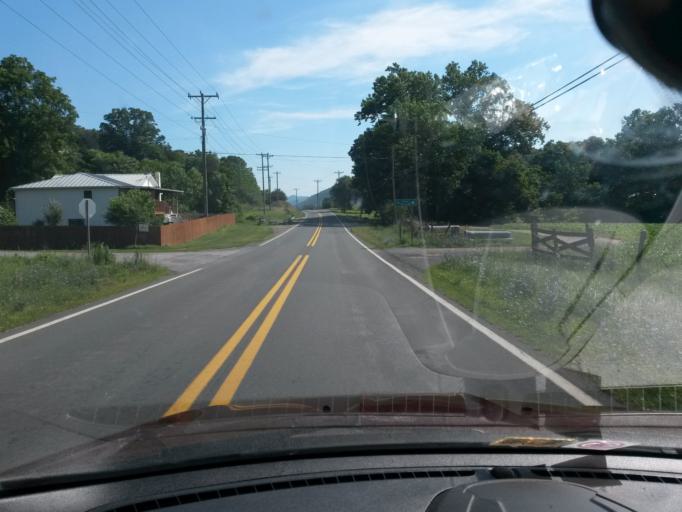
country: US
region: Virginia
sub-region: Shenandoah County
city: Basye
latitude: 38.9974
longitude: -78.7763
